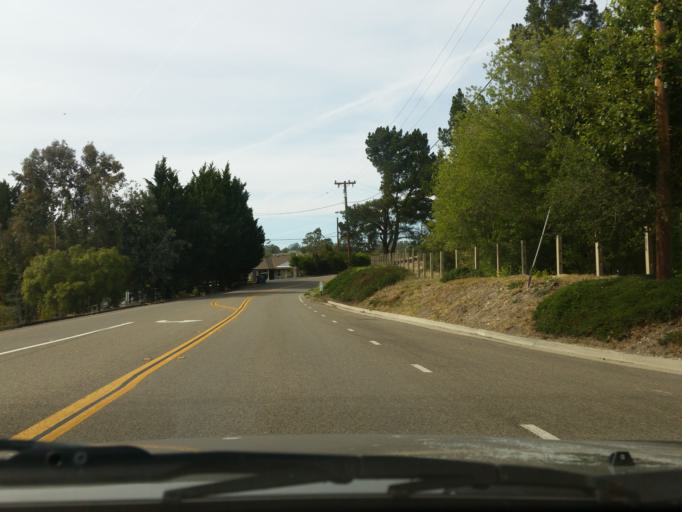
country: US
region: California
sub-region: San Luis Obispo County
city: Arroyo Grande
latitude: 35.1291
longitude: -120.5714
